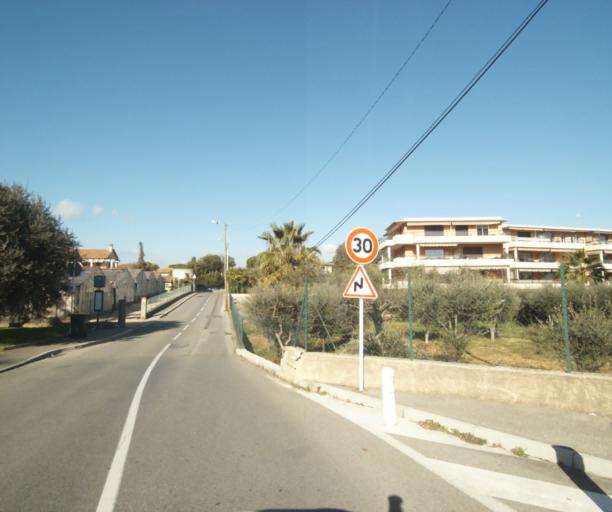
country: FR
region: Provence-Alpes-Cote d'Azur
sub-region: Departement des Alpes-Maritimes
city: Biot
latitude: 43.6030
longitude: 7.1164
